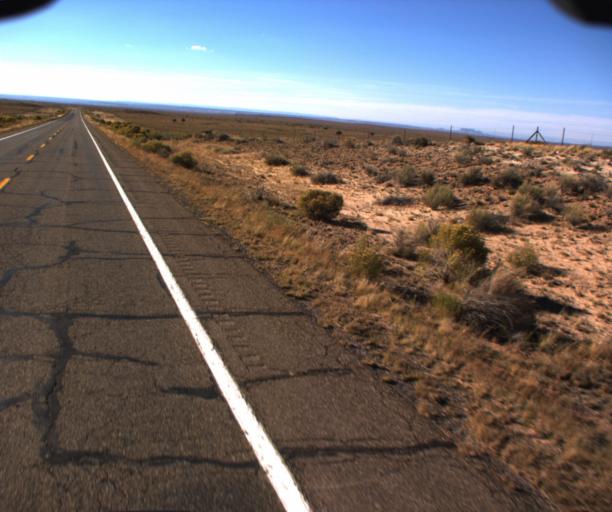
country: US
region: Arizona
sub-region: Coconino County
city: Kaibito
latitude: 36.6165
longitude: -110.9485
